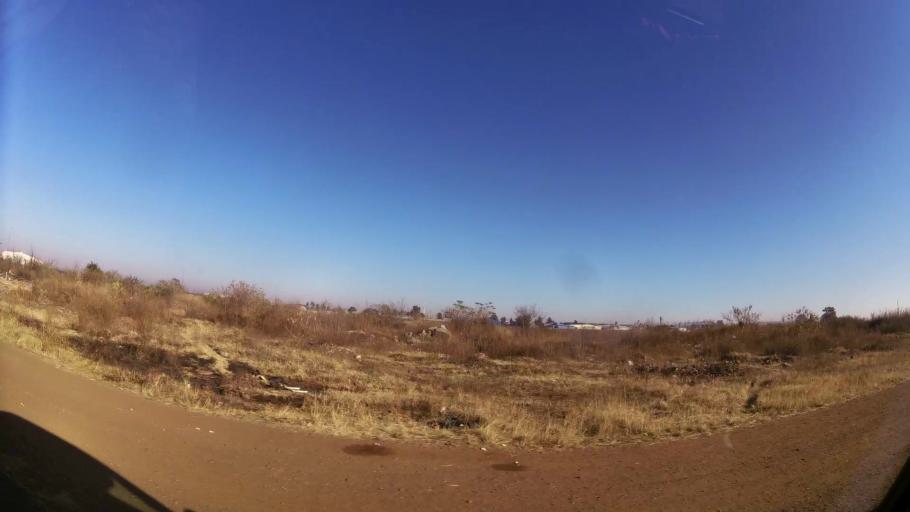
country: ZA
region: Gauteng
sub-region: Ekurhuleni Metropolitan Municipality
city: Germiston
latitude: -26.3274
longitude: 28.1383
